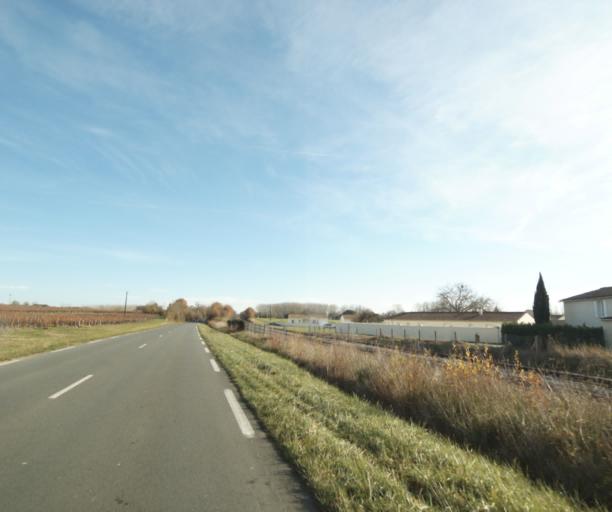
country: FR
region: Poitou-Charentes
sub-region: Departement de la Charente-Maritime
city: Chaniers
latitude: 45.7138
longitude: -0.5436
